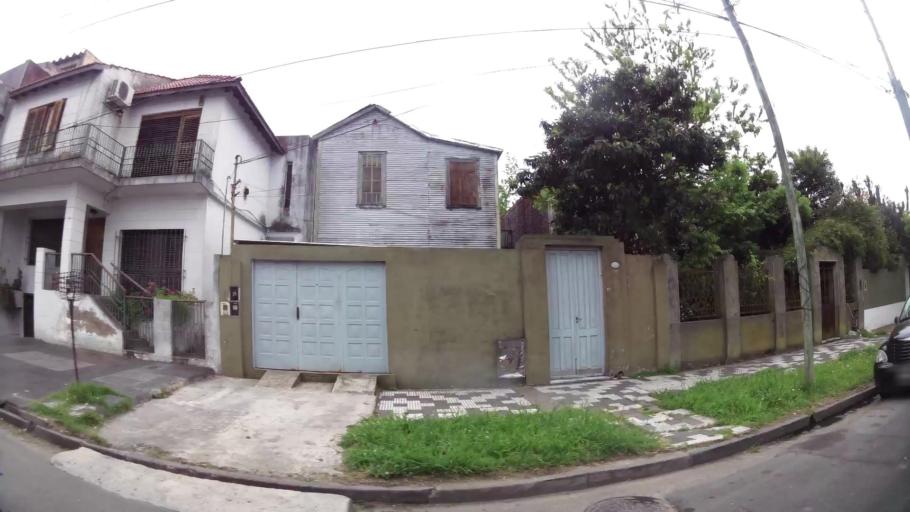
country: AR
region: Buenos Aires
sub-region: Partido de Avellaneda
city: Avellaneda
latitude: -34.6615
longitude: -58.3537
